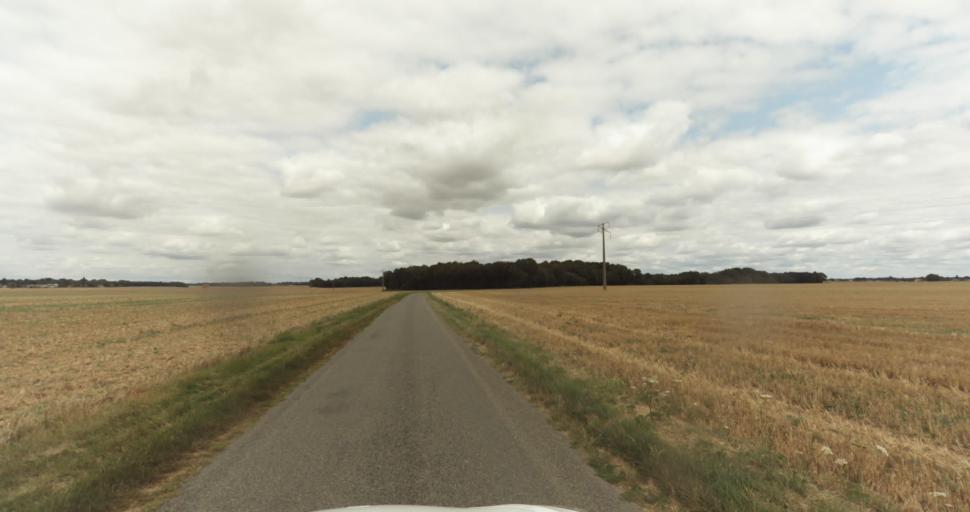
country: FR
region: Haute-Normandie
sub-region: Departement de l'Eure
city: Saint-Germain-sur-Avre
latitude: 48.8080
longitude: 1.2524
